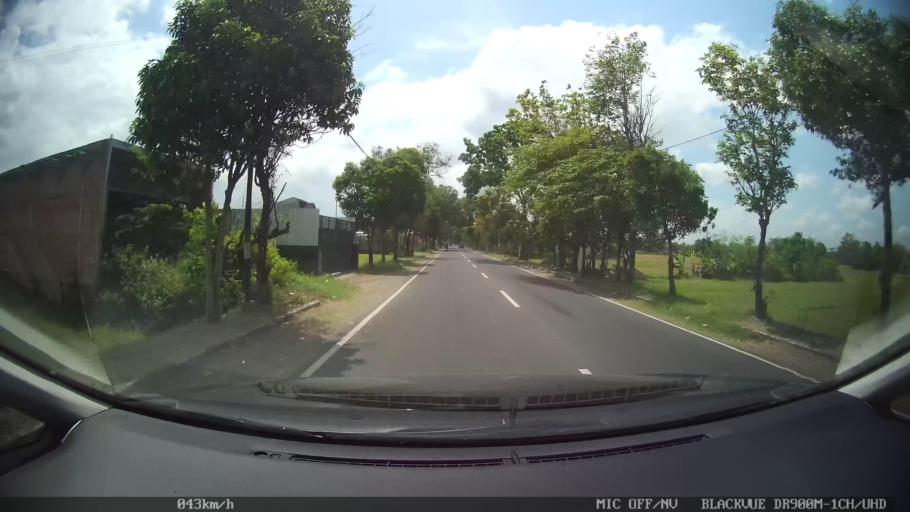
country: ID
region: Daerah Istimewa Yogyakarta
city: Bantul
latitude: -7.8892
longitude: 110.3336
